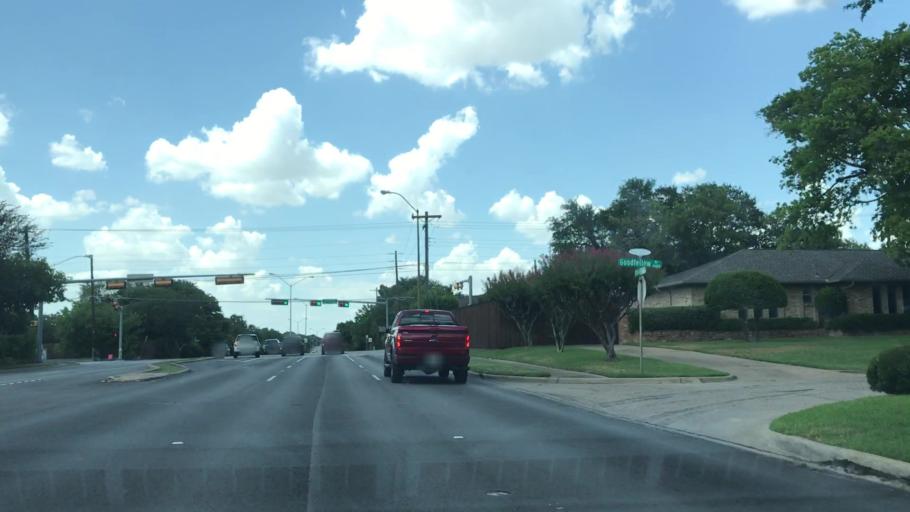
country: US
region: Texas
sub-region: Dallas County
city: Addison
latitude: 32.9088
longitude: -96.8382
